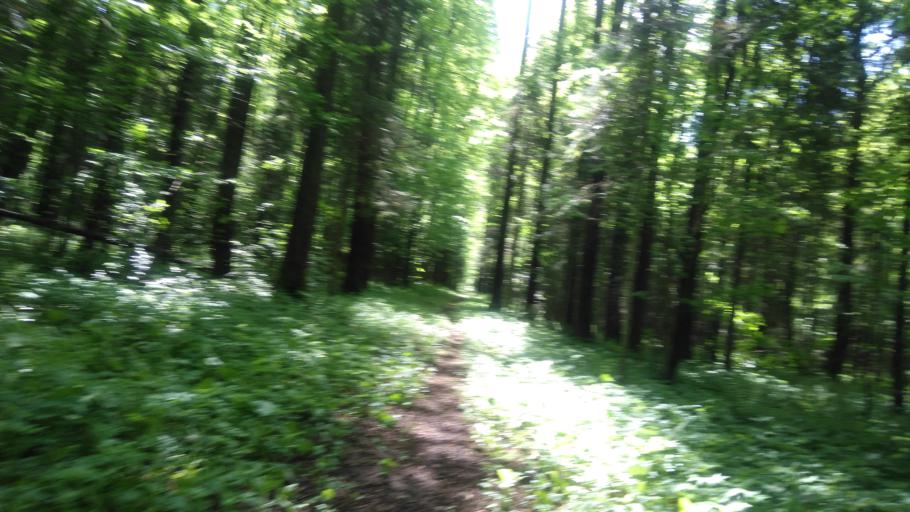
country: RU
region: Perm
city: Ferma
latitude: 57.9675
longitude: 56.3375
